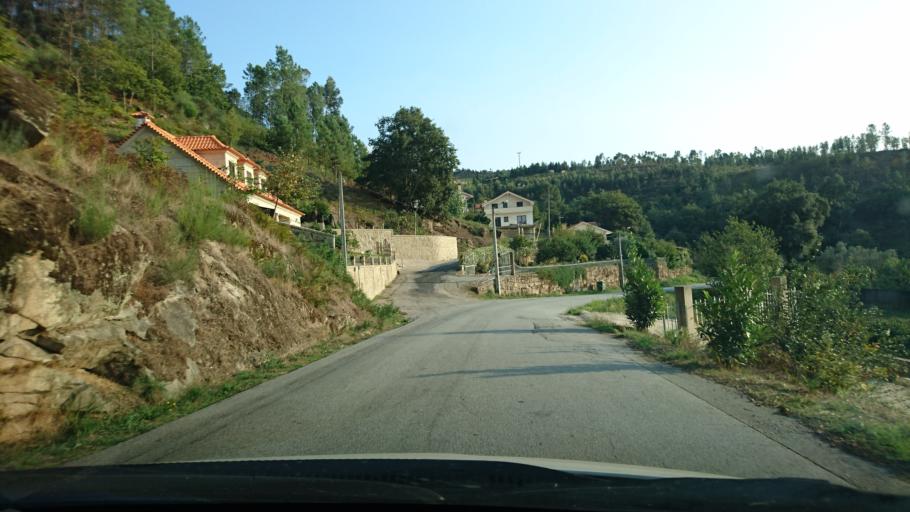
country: PT
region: Vila Real
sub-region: Mondim de Basto
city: Mondim de Basto
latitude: 41.4183
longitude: -7.9369
